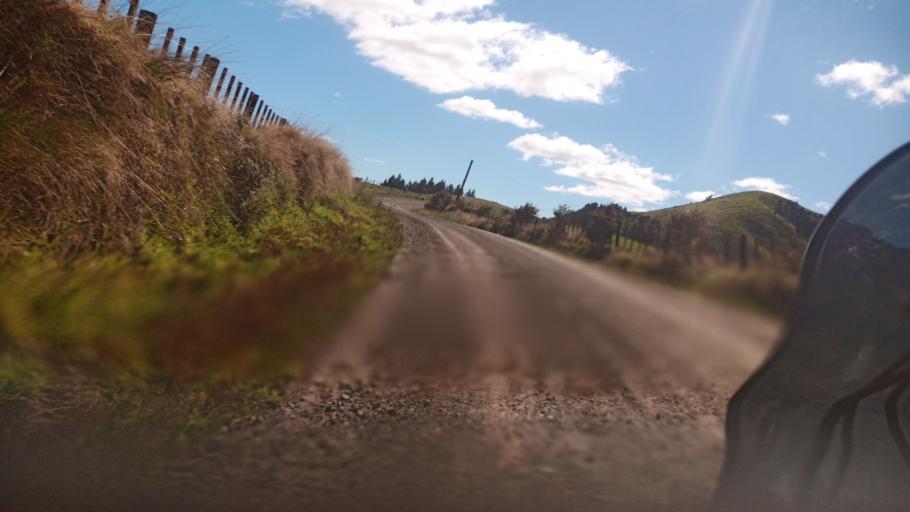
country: NZ
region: Bay of Plenty
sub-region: Opotiki District
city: Opotiki
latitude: -38.3170
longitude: 177.5698
